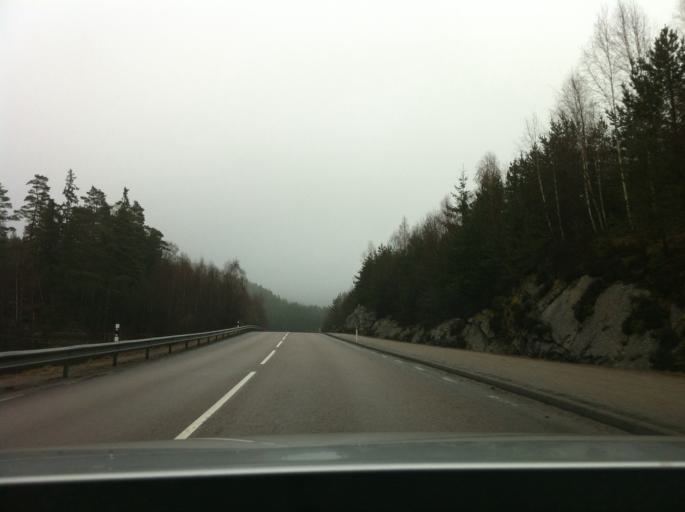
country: SE
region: Vaestra Goetaland
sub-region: Alingsas Kommun
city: Alingsas
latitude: 57.9508
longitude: 12.4854
